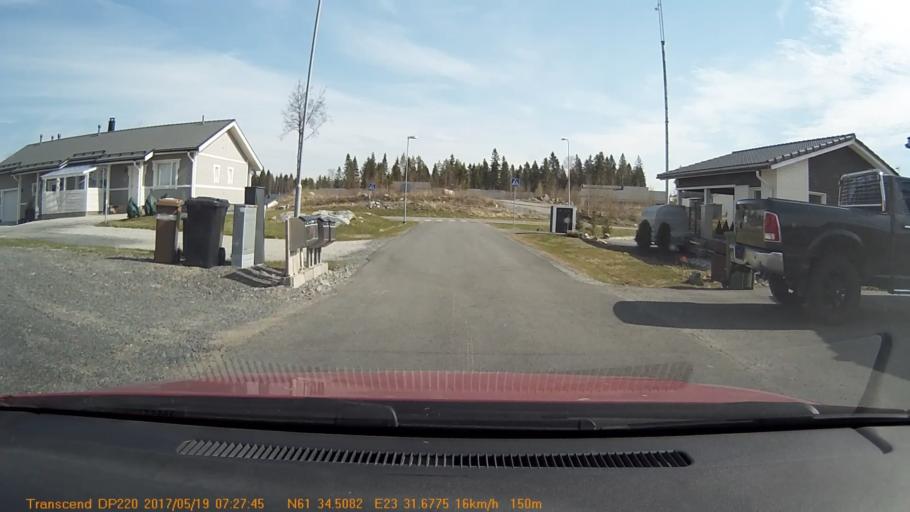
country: FI
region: Pirkanmaa
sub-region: Tampere
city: Yloejaervi
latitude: 61.5751
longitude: 23.5283
